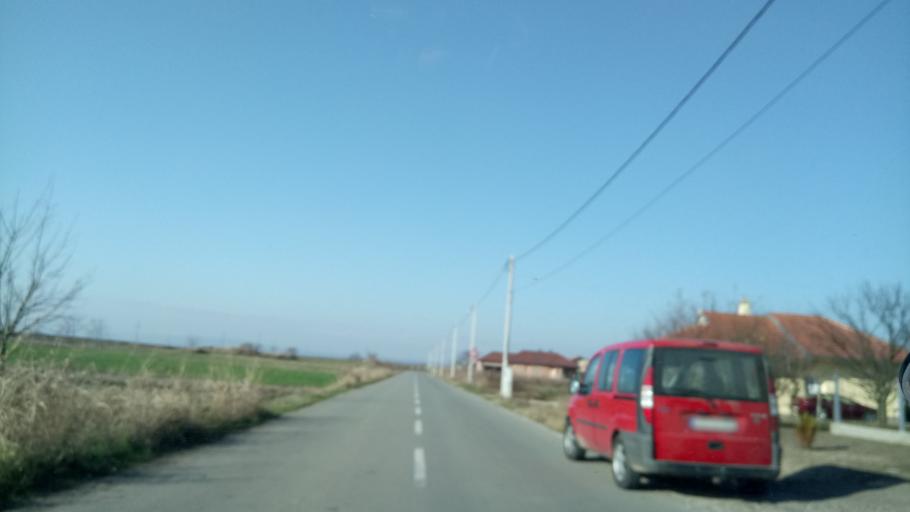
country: RS
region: Autonomna Pokrajina Vojvodina
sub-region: Sremski Okrug
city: Ingija
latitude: 45.0533
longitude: 20.0625
